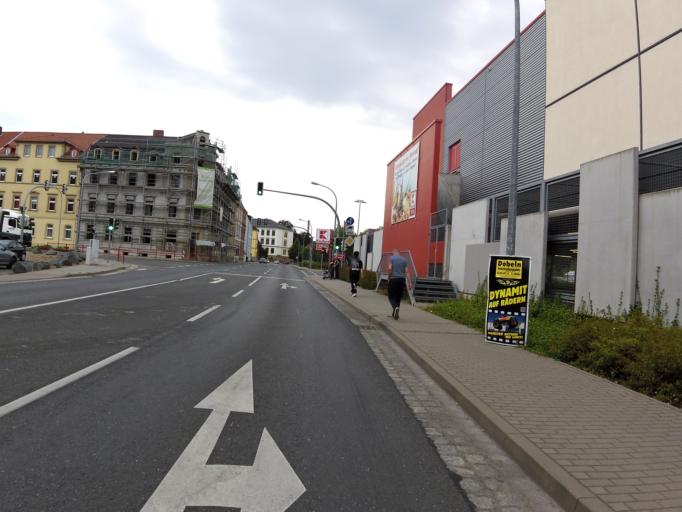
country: DE
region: Saxony
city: Dobeln
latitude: 51.1192
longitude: 13.1225
